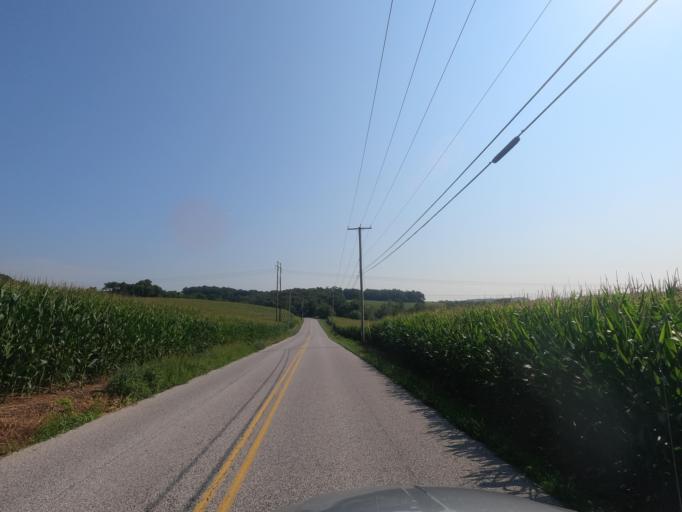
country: US
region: Pennsylvania
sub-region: York County
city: Shrewsbury
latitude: 39.7766
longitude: -76.6602
